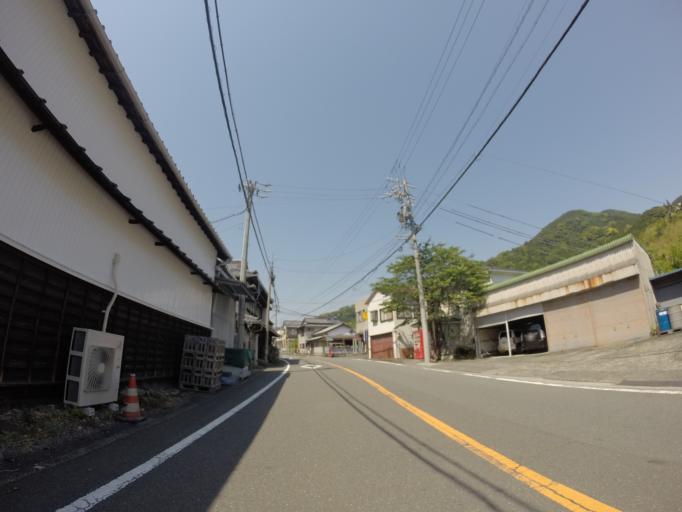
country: JP
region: Shizuoka
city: Fujinomiya
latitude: 35.1293
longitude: 138.5566
